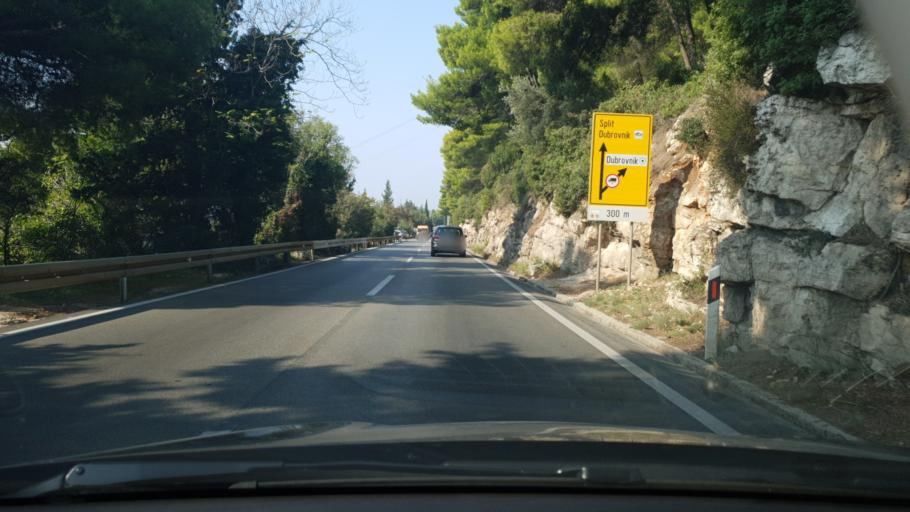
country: HR
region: Dubrovacko-Neretvanska
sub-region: Grad Dubrovnik
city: Dubrovnik
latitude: 42.6449
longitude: 18.1146
